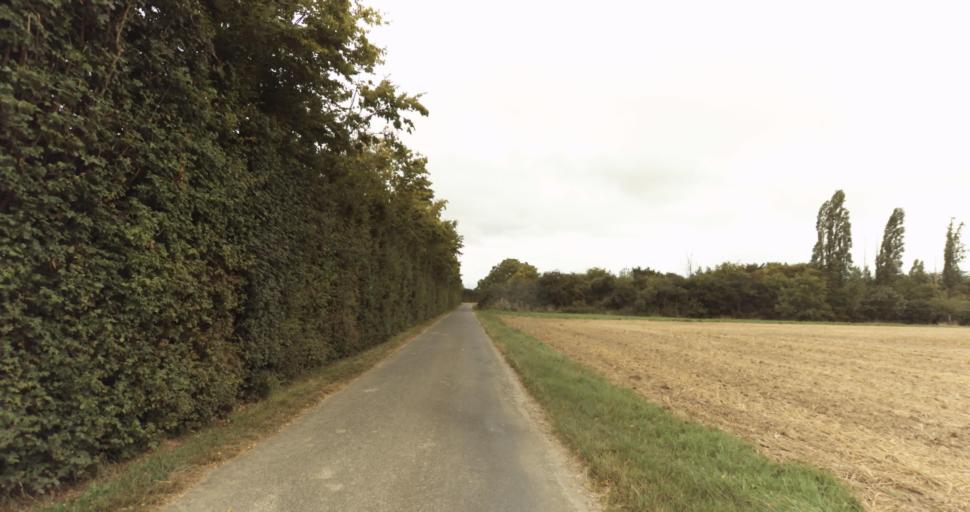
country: FR
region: Haute-Normandie
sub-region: Departement de l'Eure
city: Gravigny
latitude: 49.0347
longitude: 1.2151
